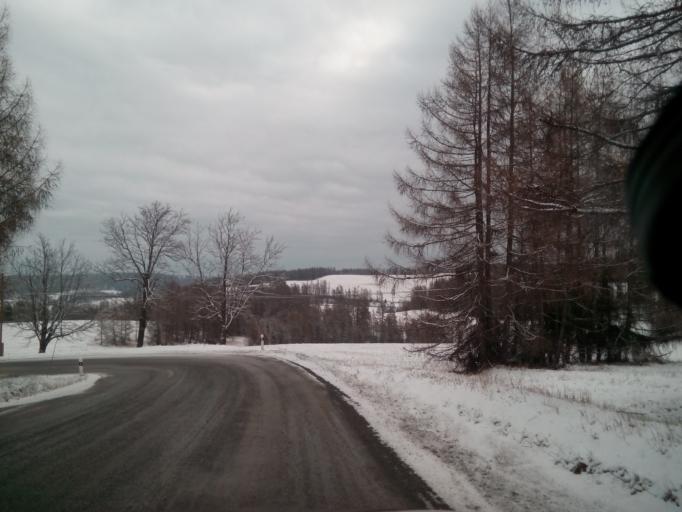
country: SK
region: Presovsky
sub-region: Okres Presov
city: Levoca
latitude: 49.0604
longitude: 20.6706
